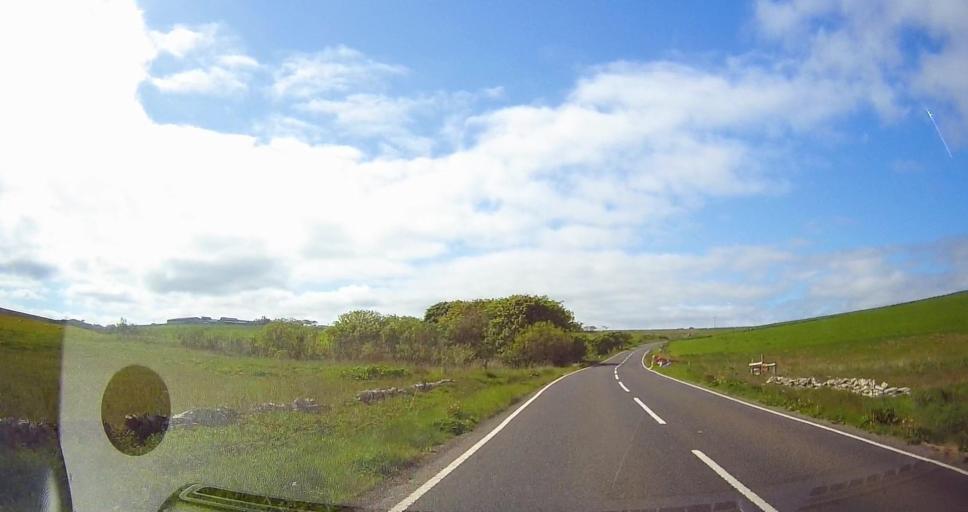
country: GB
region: Scotland
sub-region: Orkney Islands
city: Kirkwall
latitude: 58.9590
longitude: -2.9218
